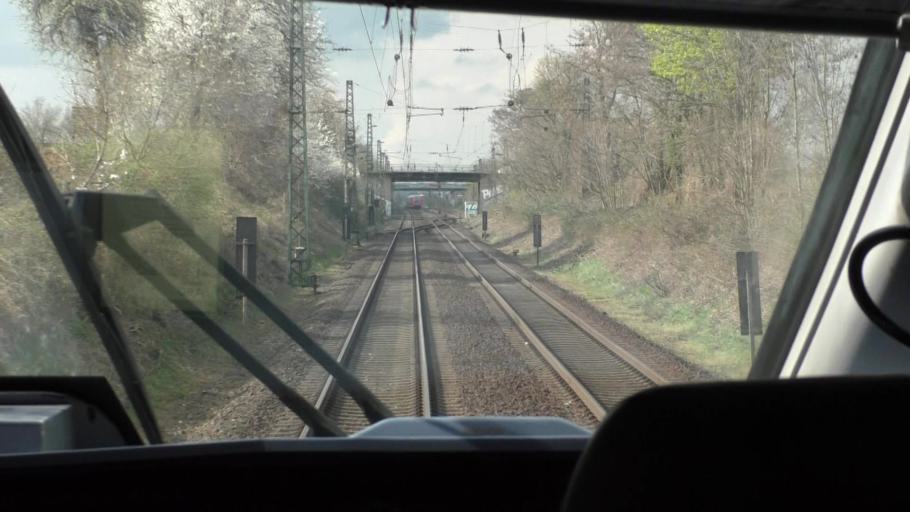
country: DE
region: North Rhine-Westphalia
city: Bornheim
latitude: 50.7894
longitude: 6.9663
